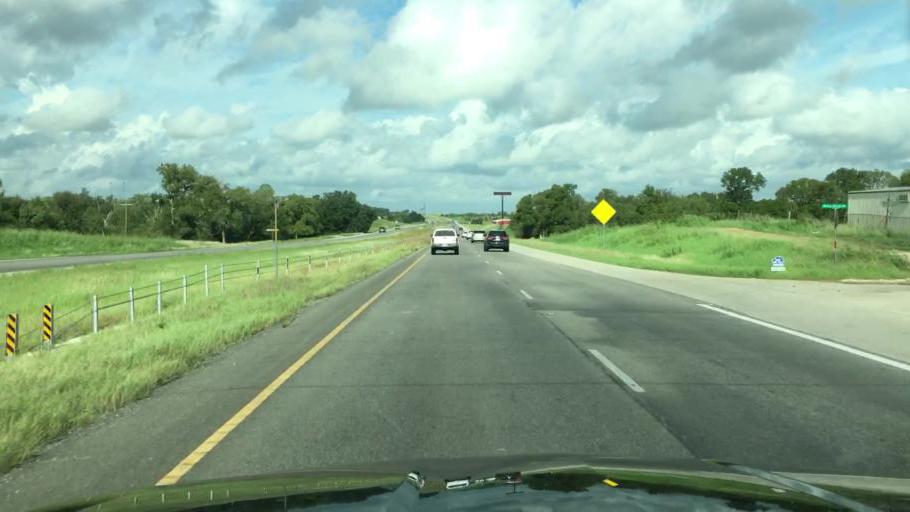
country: US
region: Texas
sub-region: Bastrop County
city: Wyldwood
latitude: 30.1623
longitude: -97.5051
